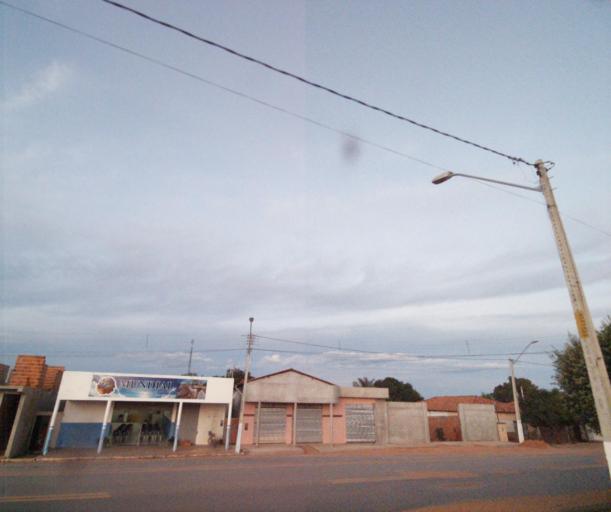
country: BR
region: Bahia
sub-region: Sao Felix Do Coribe
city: Santa Maria da Vitoria
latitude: -13.8260
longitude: -44.4605
